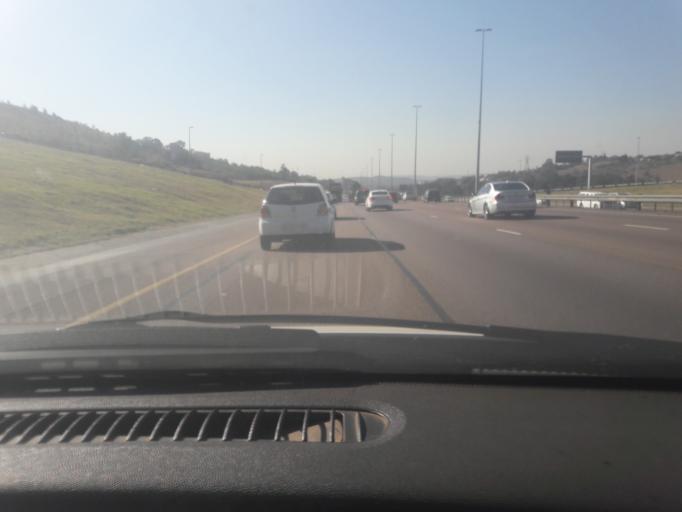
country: ZA
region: Gauteng
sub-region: City of Tshwane Metropolitan Municipality
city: Centurion
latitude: -25.8085
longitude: 28.2587
